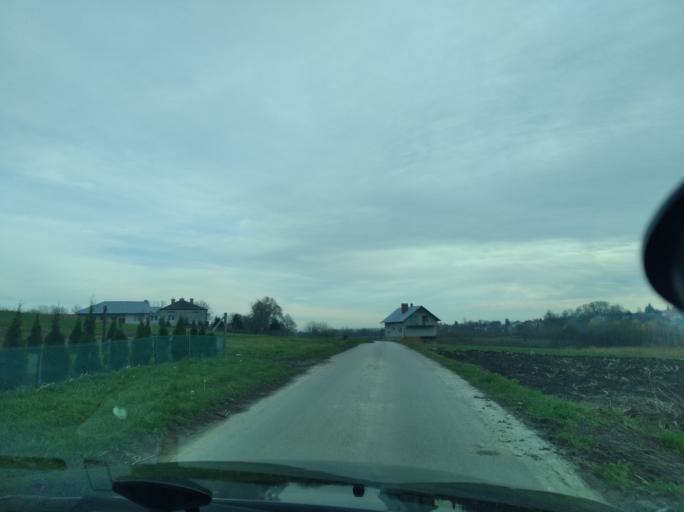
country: PL
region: Subcarpathian Voivodeship
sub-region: Powiat przeworski
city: Debow
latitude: 50.0493
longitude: 22.4246
